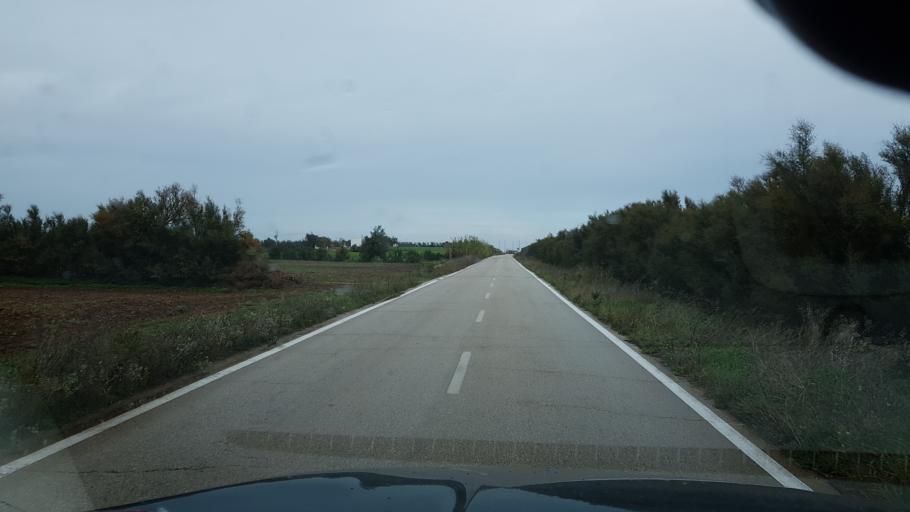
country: IT
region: Apulia
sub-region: Provincia di Brindisi
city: Brindisi
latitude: 40.6849
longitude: 17.8467
